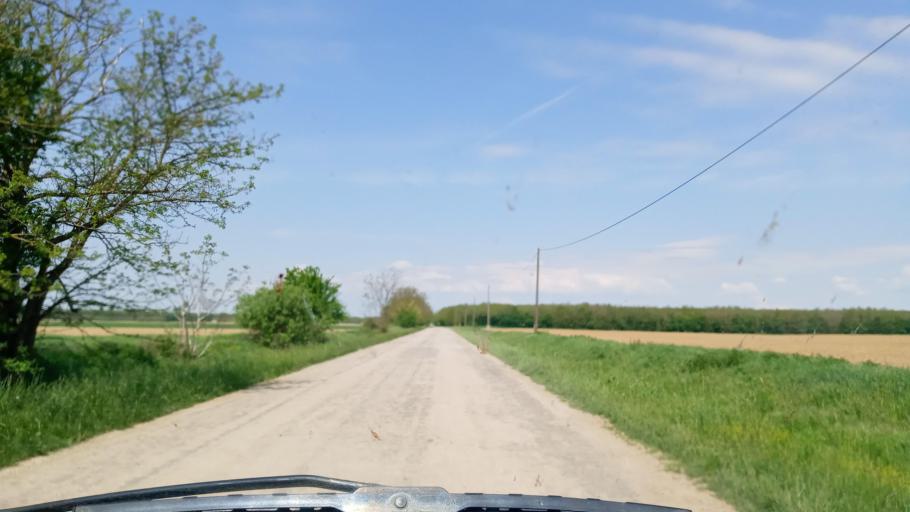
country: HU
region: Baranya
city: Boly
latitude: 45.8783
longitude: 18.5763
